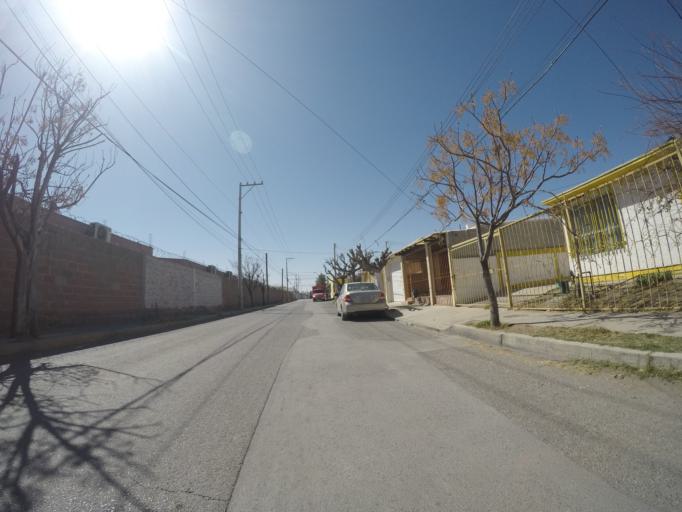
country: MX
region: Chihuahua
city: Ciudad Juarez
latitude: 31.6990
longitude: -106.4140
